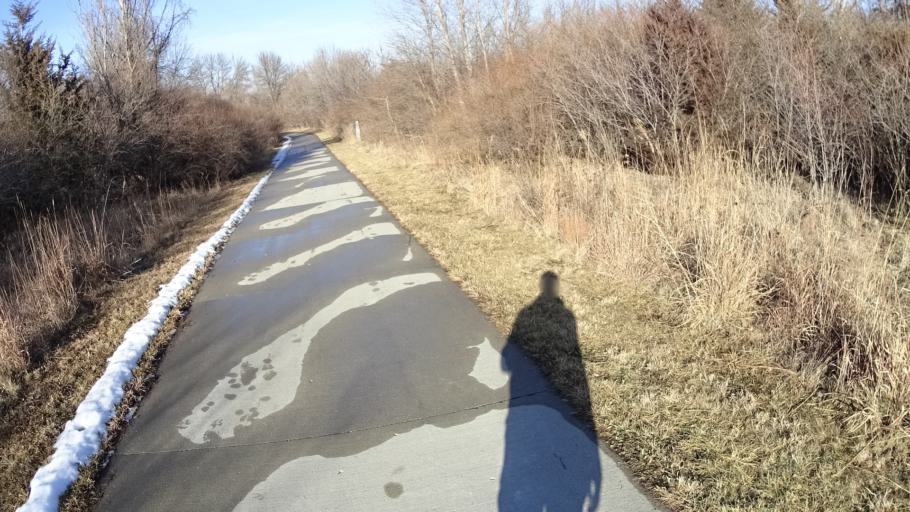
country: US
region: Nebraska
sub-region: Douglas County
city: Bennington
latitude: 41.3104
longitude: -96.1268
